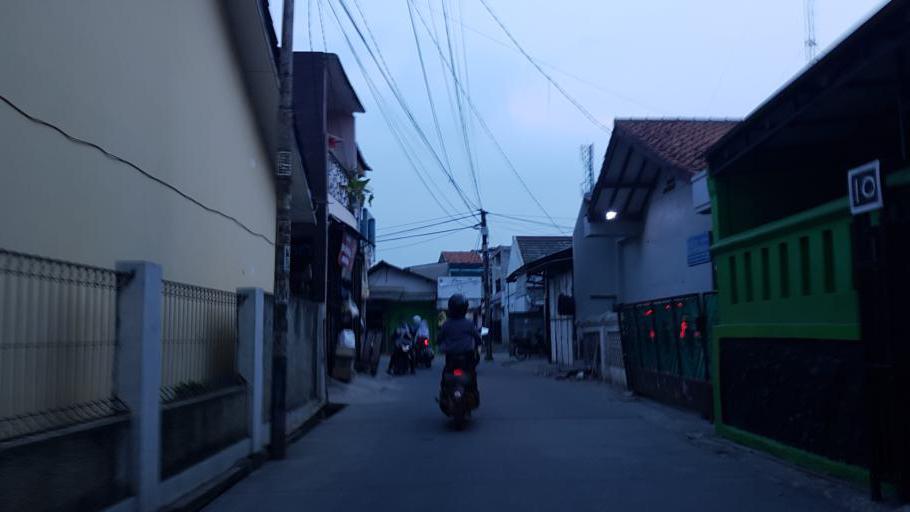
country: ID
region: West Java
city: Pamulang
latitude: -6.3279
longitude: 106.7933
